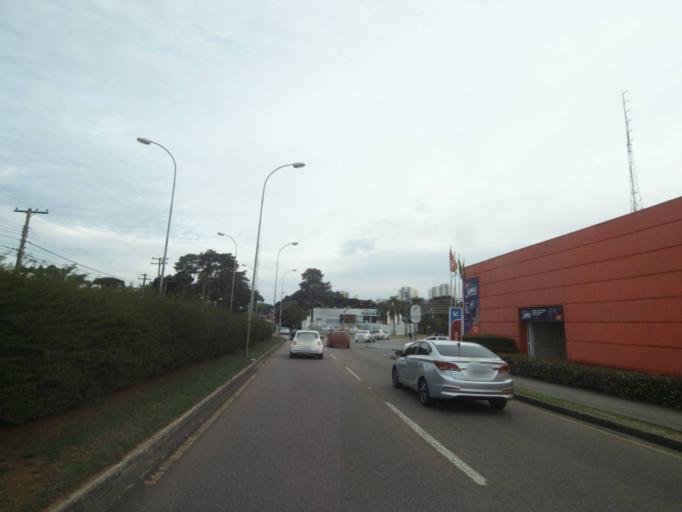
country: BR
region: Parana
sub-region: Curitiba
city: Curitiba
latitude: -25.4301
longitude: -49.2405
